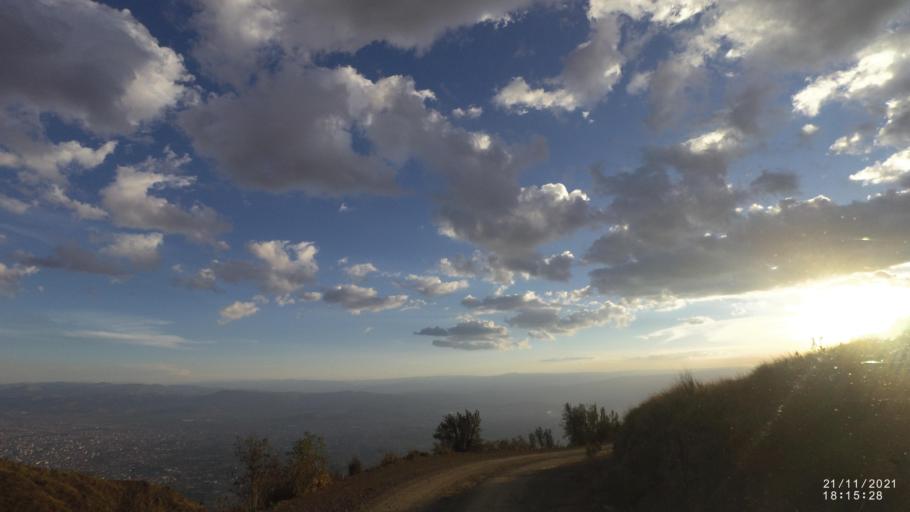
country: BO
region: Cochabamba
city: Cochabamba
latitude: -17.2884
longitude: -66.2135
